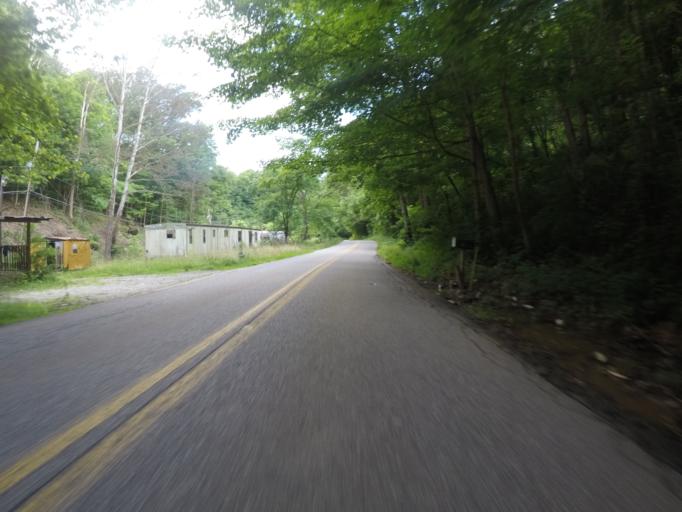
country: US
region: West Virginia
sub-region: Cabell County
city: Pea Ridge
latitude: 38.3917
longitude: -82.3603
